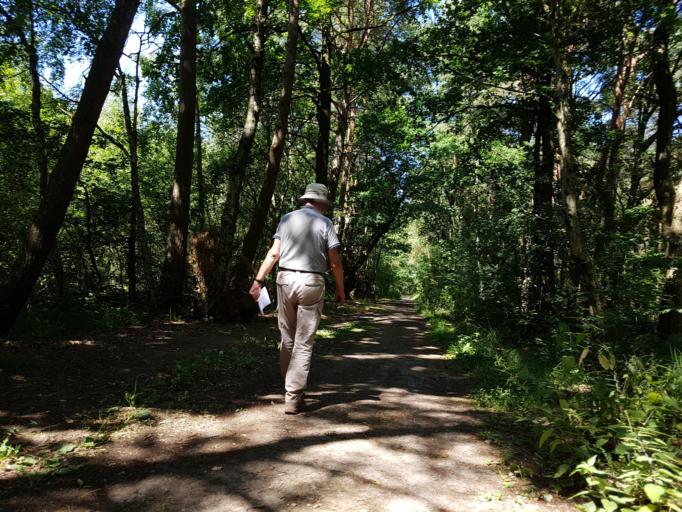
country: NL
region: North Brabant
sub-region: Gemeente Haaren
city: Haaren
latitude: 51.5730
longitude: 5.2370
